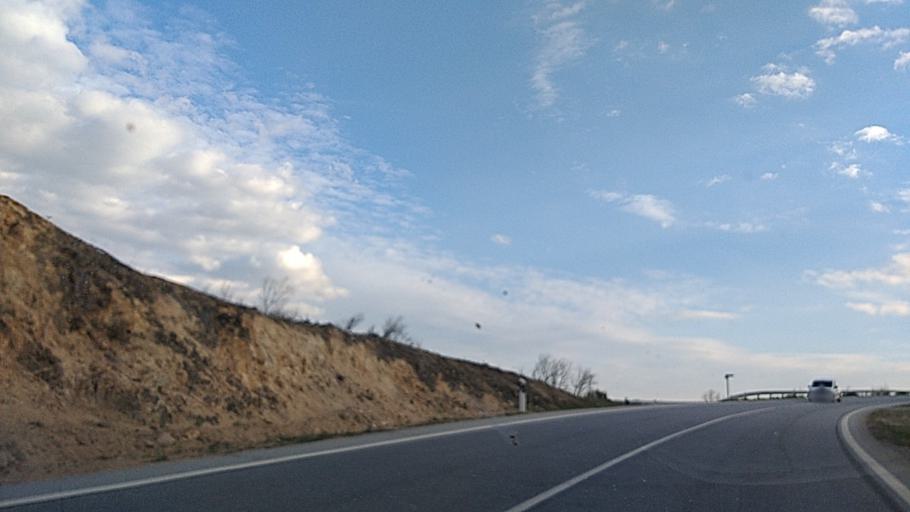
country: ES
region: Castille and Leon
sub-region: Provincia de Salamanca
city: Aldea del Obispo
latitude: 40.6989
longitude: -6.9335
